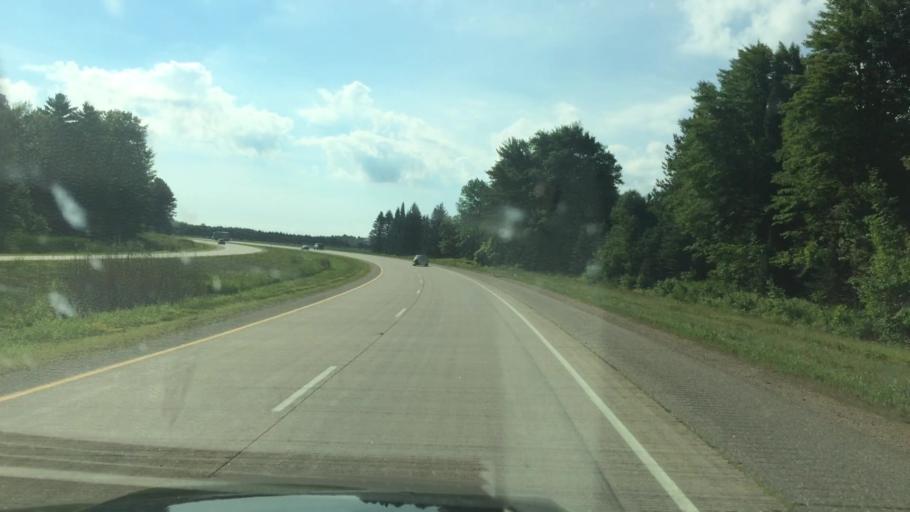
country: US
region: Wisconsin
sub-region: Shawano County
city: Wittenberg
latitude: 44.8052
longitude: -89.0339
